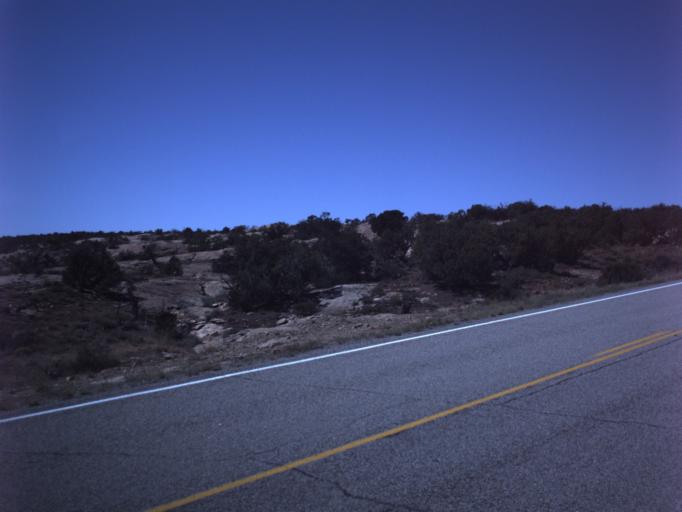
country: US
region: Utah
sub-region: San Juan County
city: Blanding
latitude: 37.5282
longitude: -109.6887
